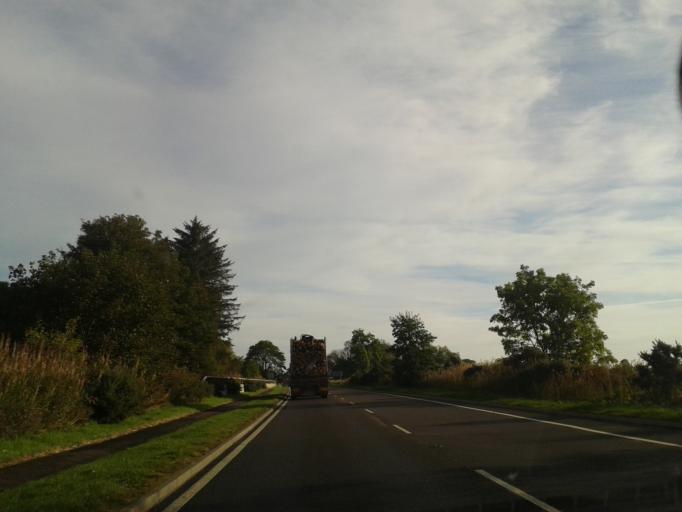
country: GB
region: Scotland
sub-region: Highland
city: Inverness
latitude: 57.4919
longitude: -4.1590
